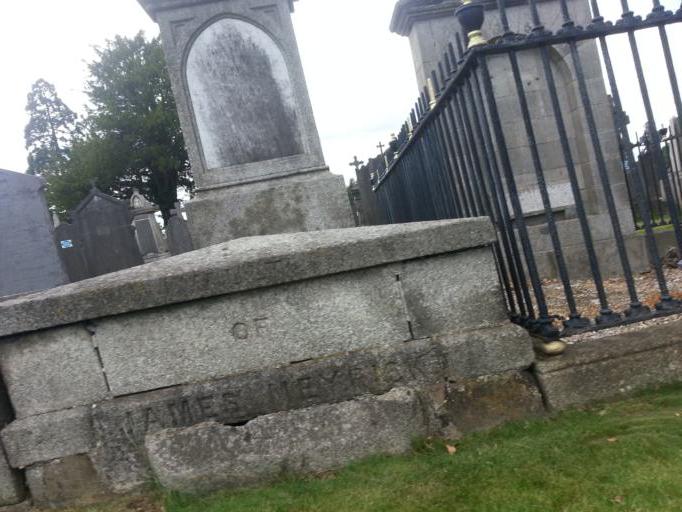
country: IE
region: Leinster
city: Glasnevin
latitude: 53.3700
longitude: -6.2757
